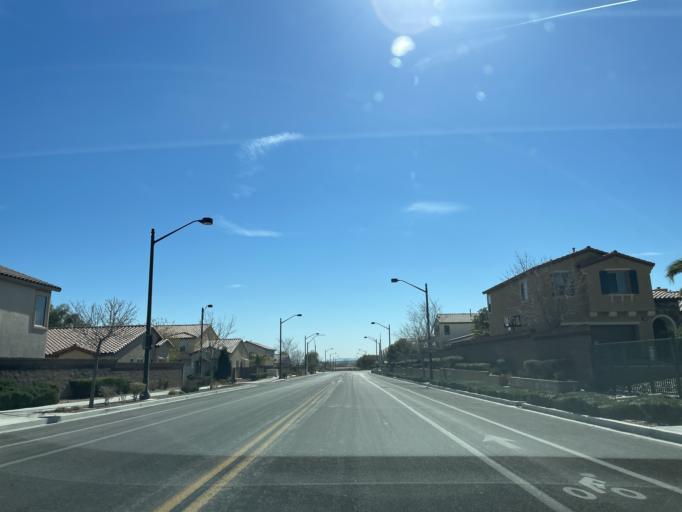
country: US
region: Nevada
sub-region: Clark County
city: Summerlin South
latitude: 36.2862
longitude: -115.3015
